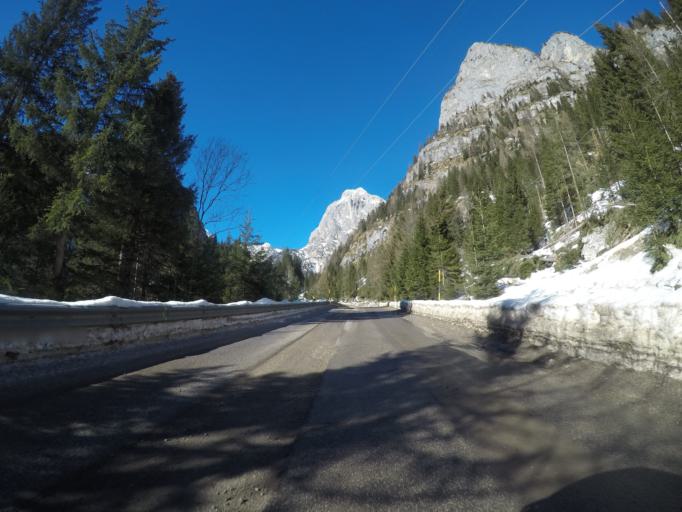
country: IT
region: Veneto
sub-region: Provincia di Belluno
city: Rocca Pietore
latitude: 46.4256
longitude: 11.9243
